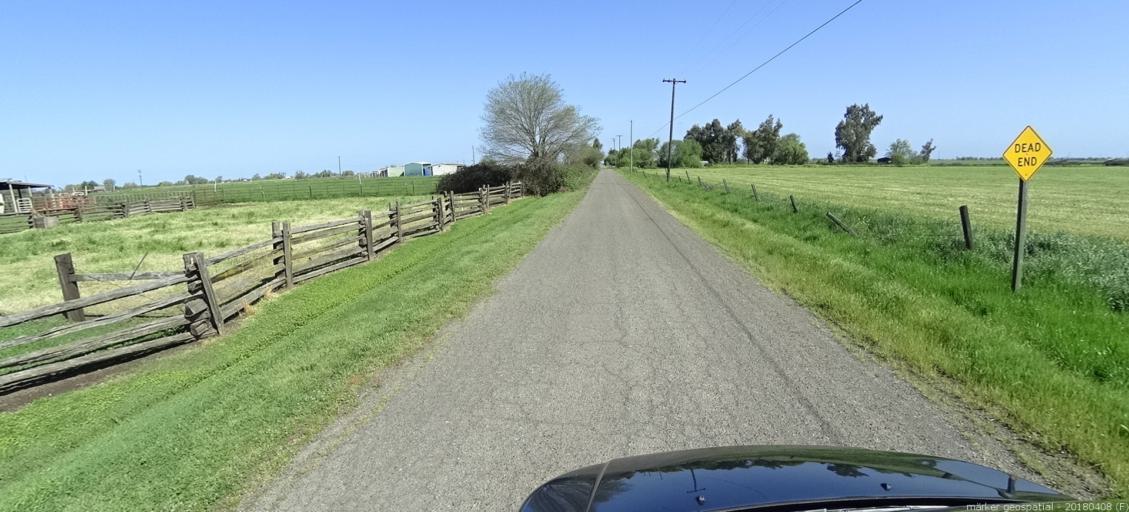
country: US
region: California
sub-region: Sacramento County
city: Laguna
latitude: 38.3372
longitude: -121.4638
